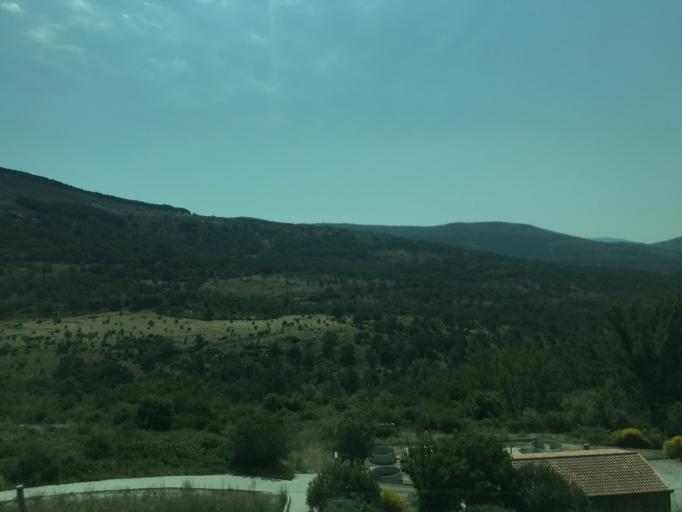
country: ES
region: Madrid
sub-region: Provincia de Madrid
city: Robregordo
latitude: 41.1048
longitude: -3.5919
